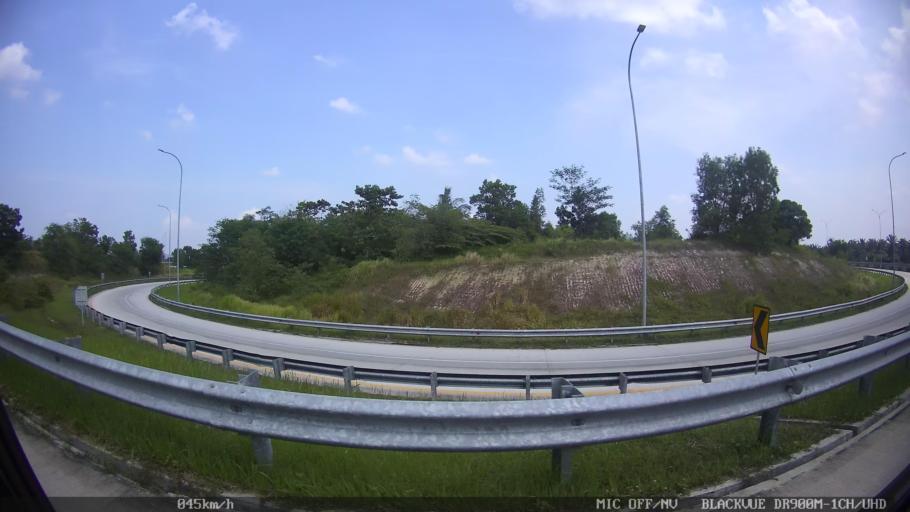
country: ID
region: Lampung
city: Natar
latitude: -5.2746
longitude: 105.2176
